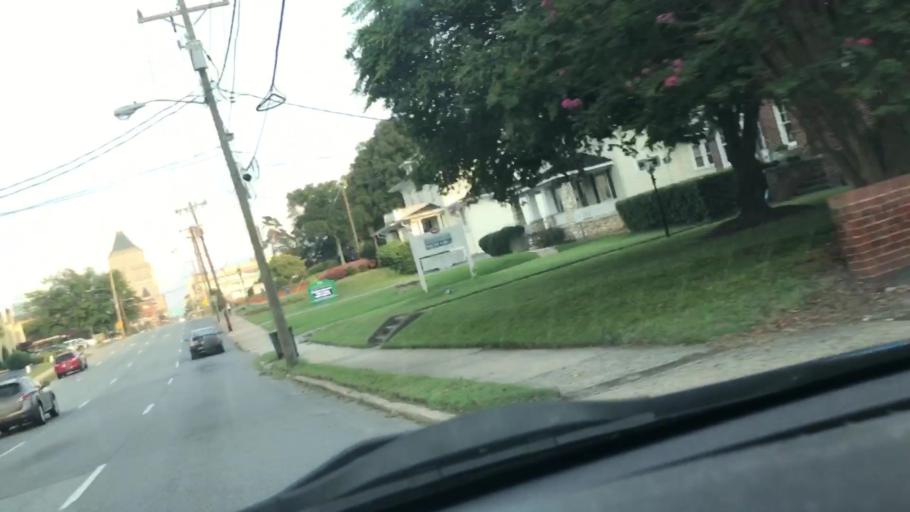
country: US
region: North Carolina
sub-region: Guilford County
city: Greensboro
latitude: 36.0730
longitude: -79.8022
